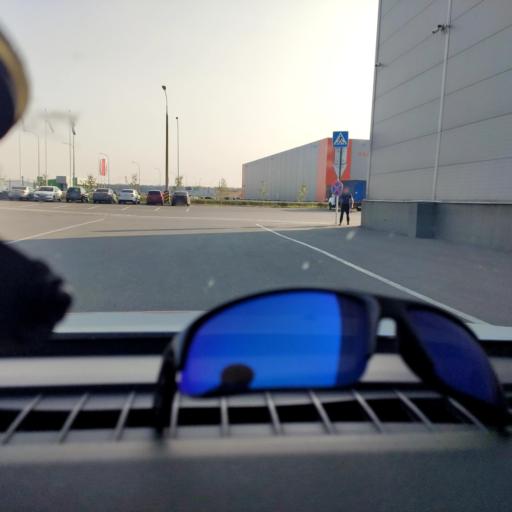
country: RU
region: Samara
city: Samara
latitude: 53.0941
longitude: 50.1342
